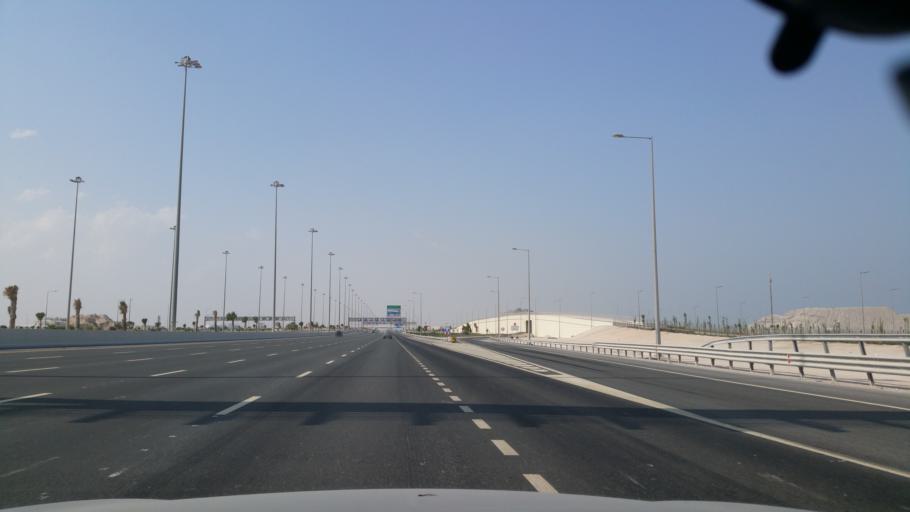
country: QA
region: Baladiyat Umm Salal
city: Umm Salal Muhammad
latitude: 25.4444
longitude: 51.4814
